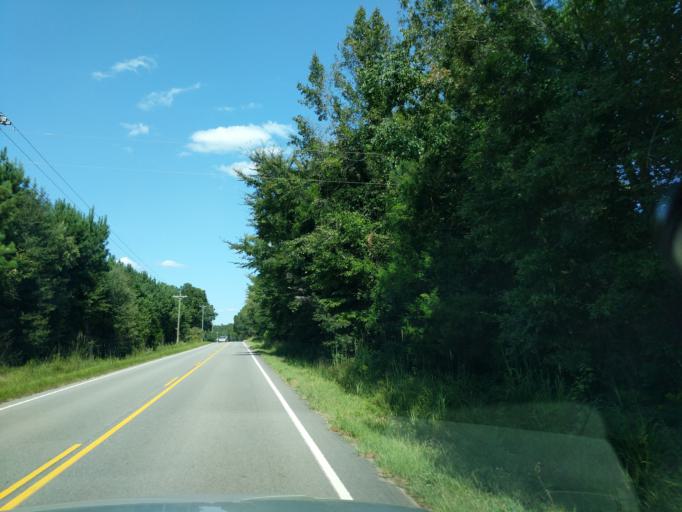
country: US
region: South Carolina
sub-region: Newberry County
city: Prosperity
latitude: 34.1240
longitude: -81.5483
